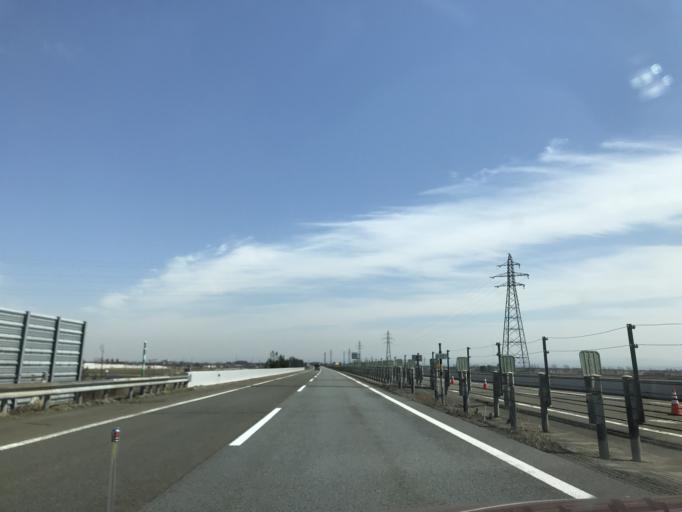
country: JP
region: Hokkaido
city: Ebetsu
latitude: 43.0842
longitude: 141.5580
